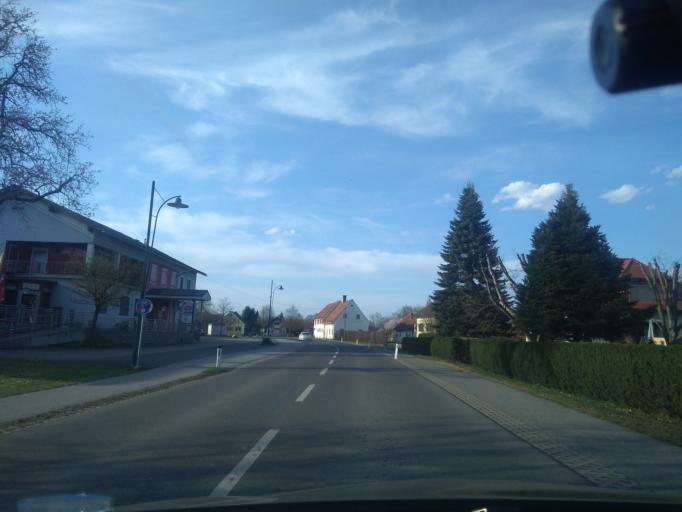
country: AT
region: Styria
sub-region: Politischer Bezirk Suedoststeiermark
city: Eichfeld
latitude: 46.7246
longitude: 15.7696
